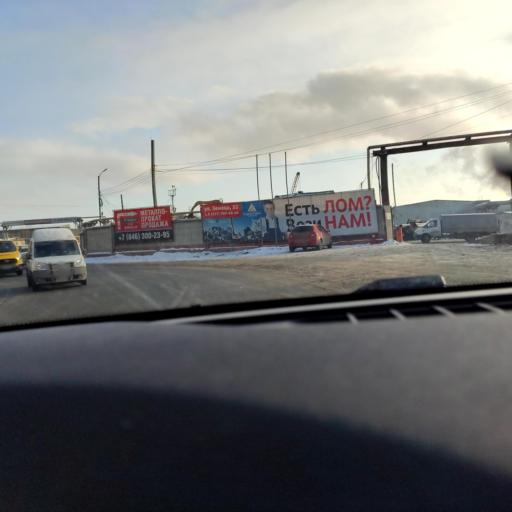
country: RU
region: Samara
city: Smyshlyayevka
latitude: 53.2107
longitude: 50.2978
